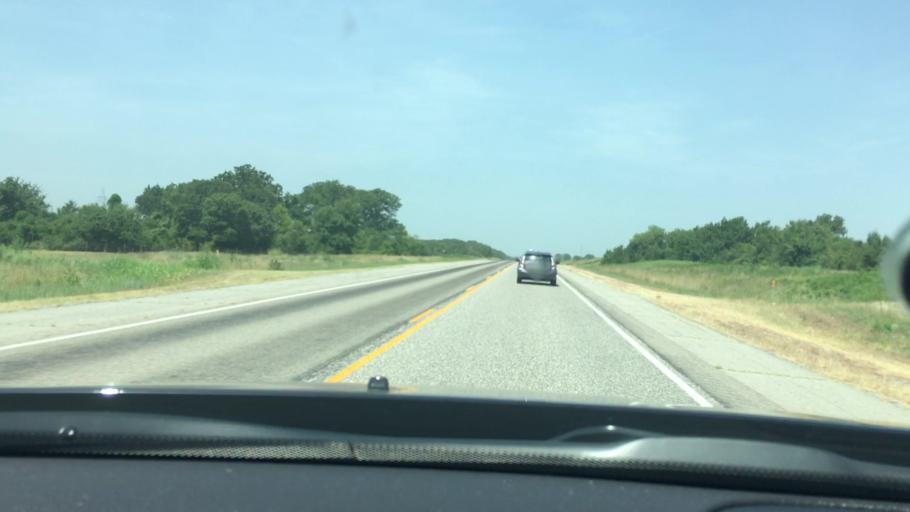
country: US
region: Oklahoma
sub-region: Coal County
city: Coalgate
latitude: 34.6002
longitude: -96.3397
